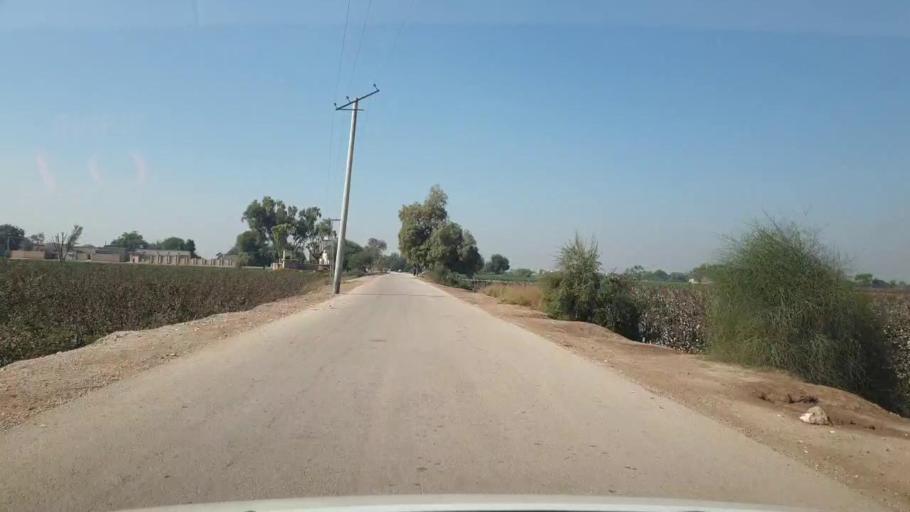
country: PK
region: Sindh
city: Bhan
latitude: 26.6460
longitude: 67.7198
